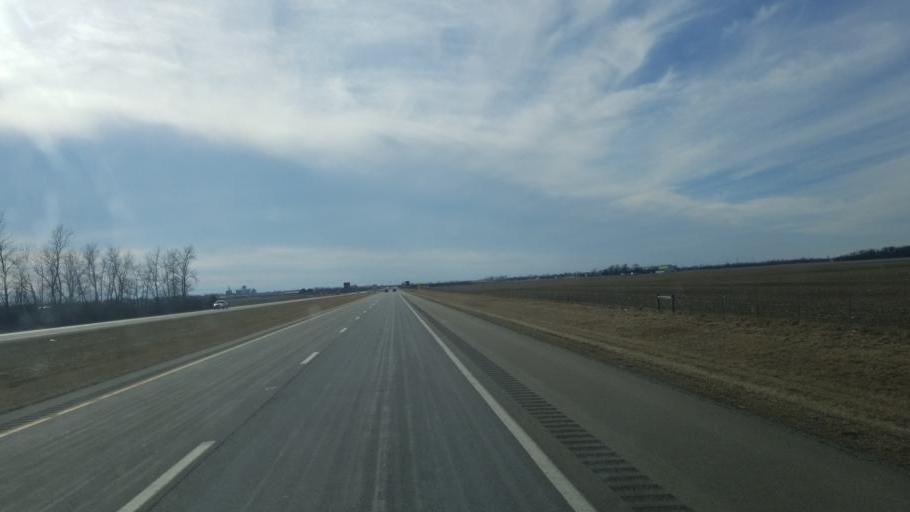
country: US
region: Ohio
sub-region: Van Wert County
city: Van Wert
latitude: 40.8853
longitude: -84.5474
